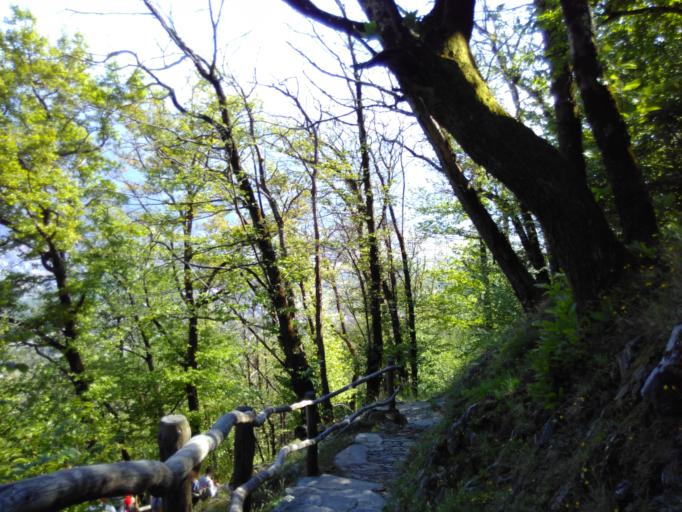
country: CH
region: Ticino
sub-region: Bellinzona District
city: Monte Carasso
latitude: 46.1939
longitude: 8.9925
